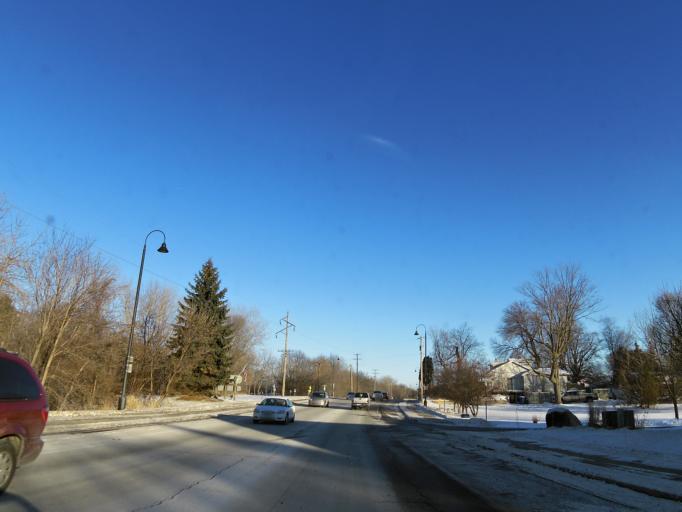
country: US
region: Minnesota
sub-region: Hennepin County
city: Mound
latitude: 44.9370
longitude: -93.6493
